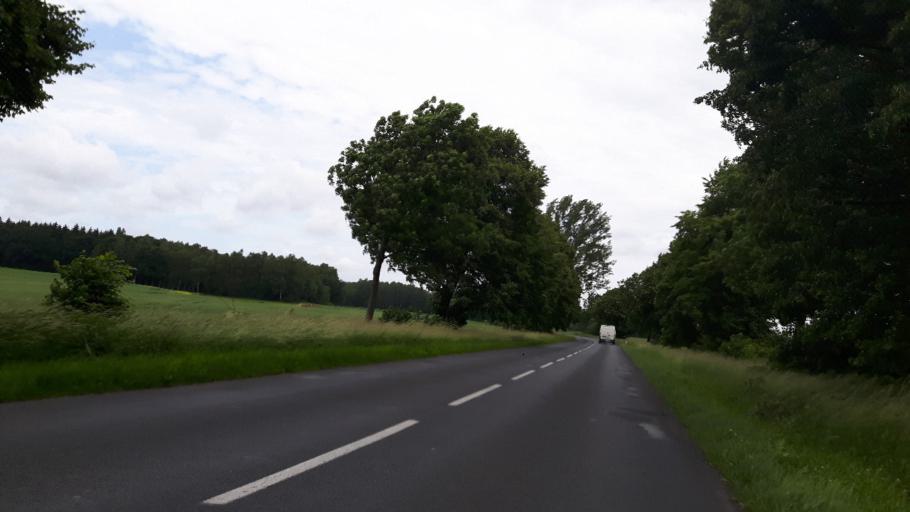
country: PL
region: West Pomeranian Voivodeship
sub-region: Powiat gryficki
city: Gryfice
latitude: 53.9819
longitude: 15.2387
